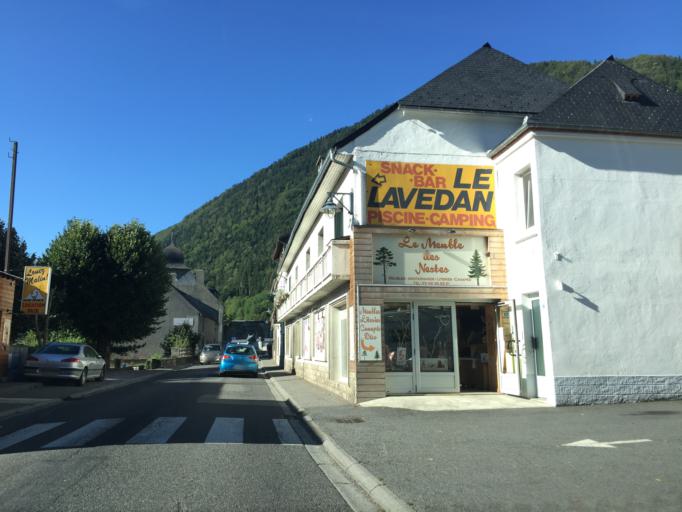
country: FR
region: Midi-Pyrenees
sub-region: Departement des Hautes-Pyrenees
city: Saint-Lary-Soulan
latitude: 42.8644
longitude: 0.3388
